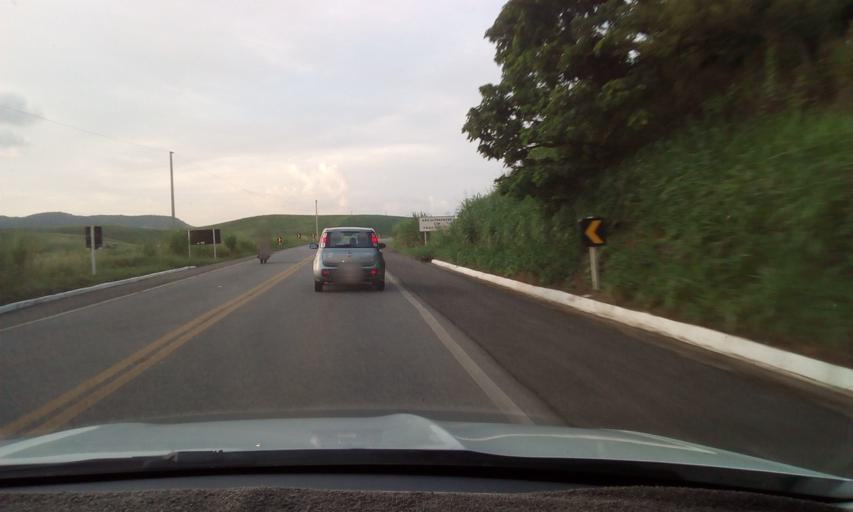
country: BR
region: Pernambuco
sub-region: Vicencia
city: Vicencia
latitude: -7.6217
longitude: -35.2412
